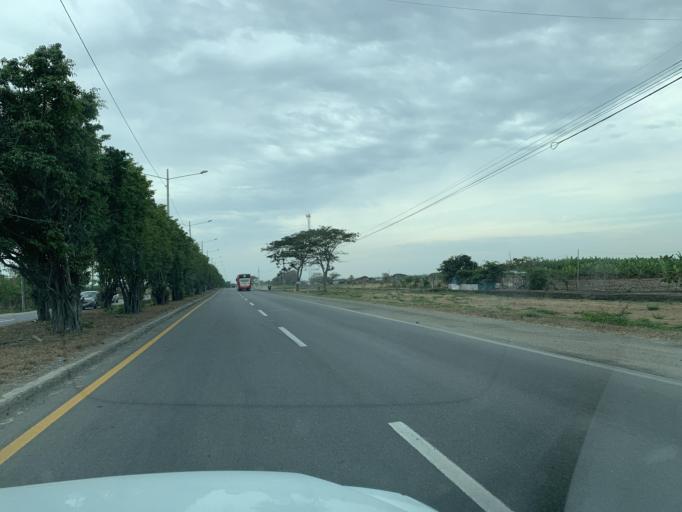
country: EC
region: Guayas
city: Yaguachi Nuevo
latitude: -2.2100
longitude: -79.7239
